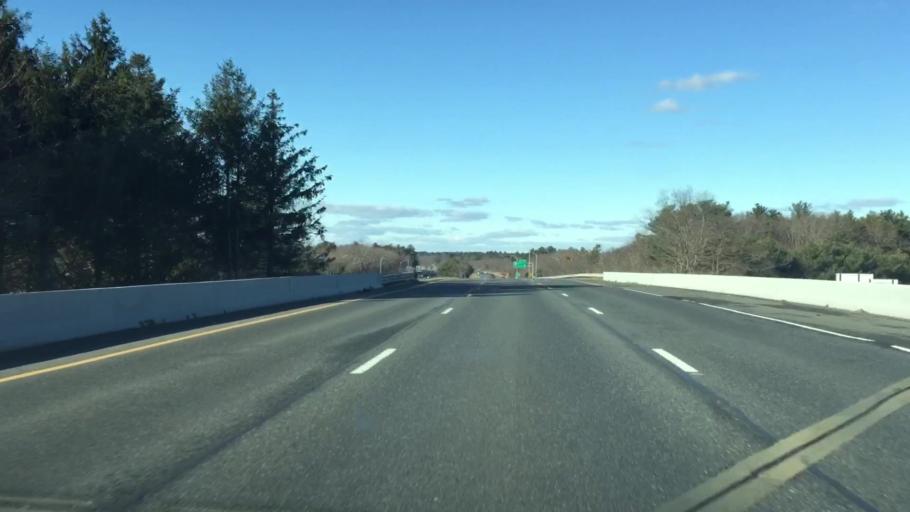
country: US
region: Massachusetts
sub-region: Bristol County
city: Raynham Center
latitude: 41.9492
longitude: -71.0238
